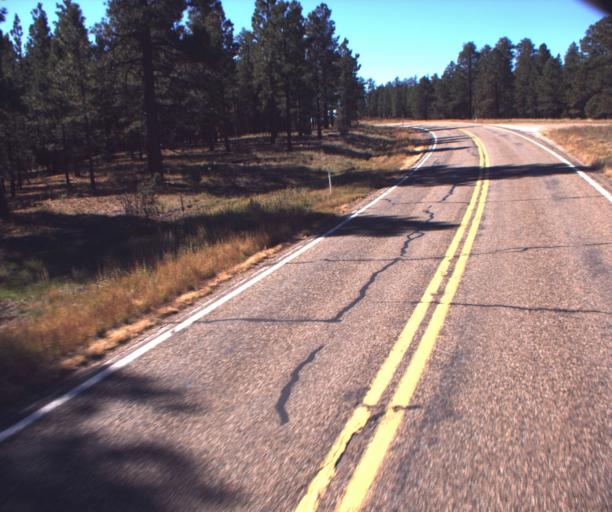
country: US
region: Arizona
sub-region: Coconino County
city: Fredonia
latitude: 36.7621
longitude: -112.2637
